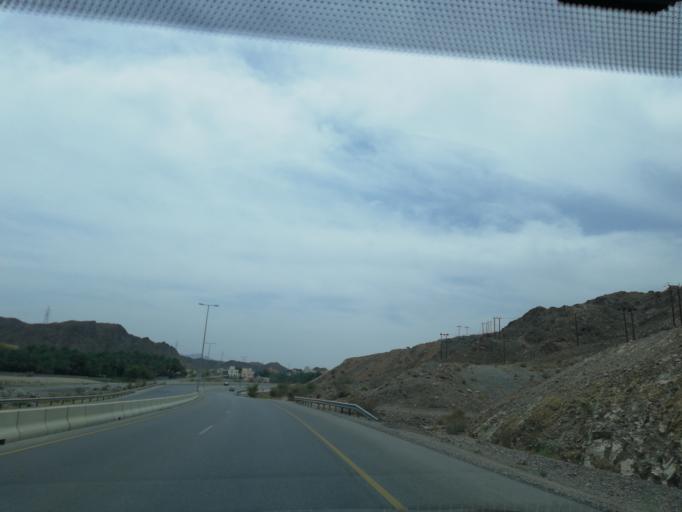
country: OM
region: Muhafazat ad Dakhiliyah
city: Izki
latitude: 23.1252
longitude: 57.8390
